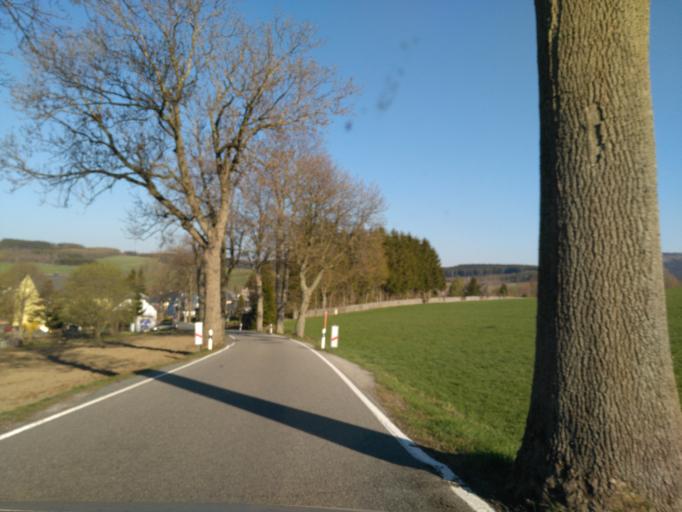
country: DE
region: Saxony
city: Schlettau
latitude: 50.5382
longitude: 12.9859
